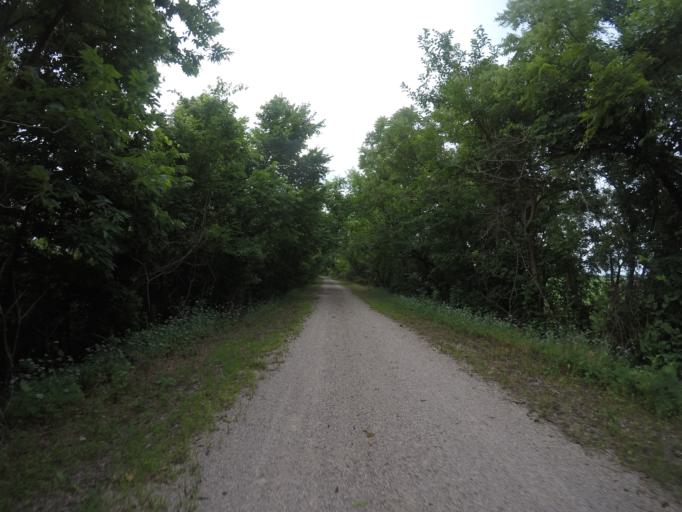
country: US
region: Kansas
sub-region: Franklin County
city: Ottawa
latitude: 38.4803
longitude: -95.2751
